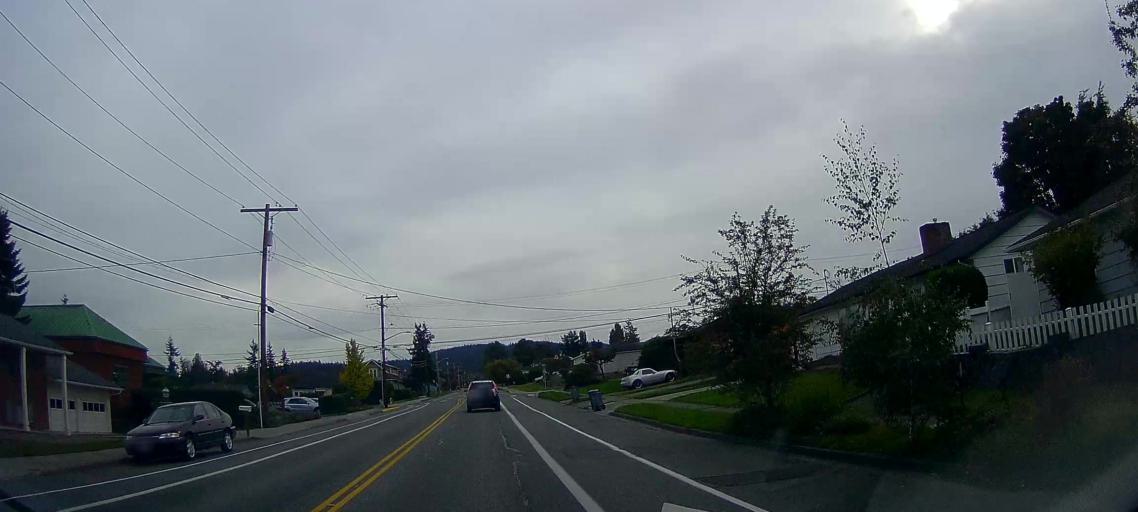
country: US
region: Washington
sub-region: Skagit County
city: Anacortes
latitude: 48.4997
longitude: -122.6175
